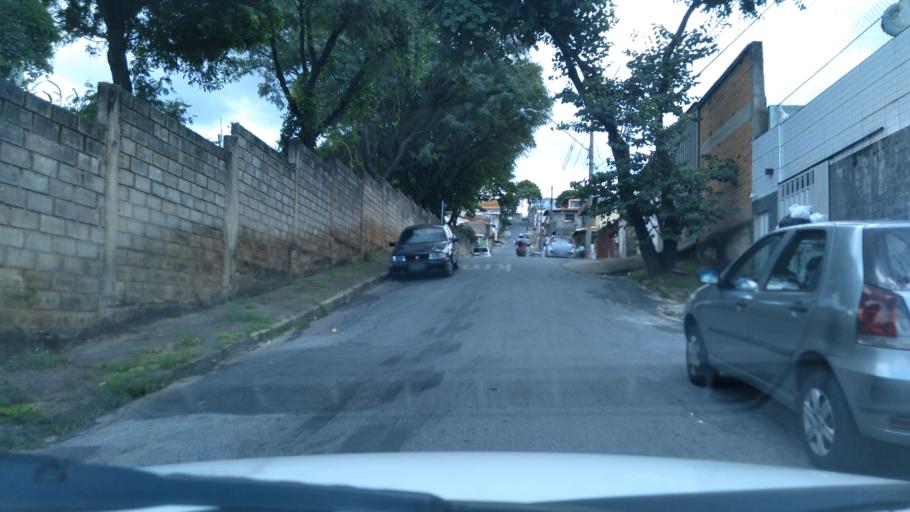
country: BR
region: Minas Gerais
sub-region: Belo Horizonte
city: Belo Horizonte
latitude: -19.9135
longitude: -43.8953
